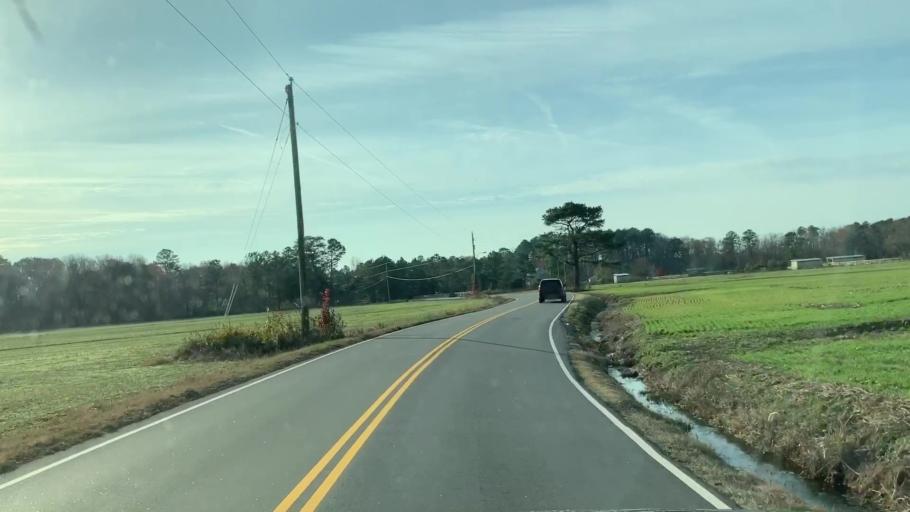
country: US
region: Virginia
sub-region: City of Virginia Beach
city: Virginia Beach
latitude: 36.7154
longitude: -76.0498
